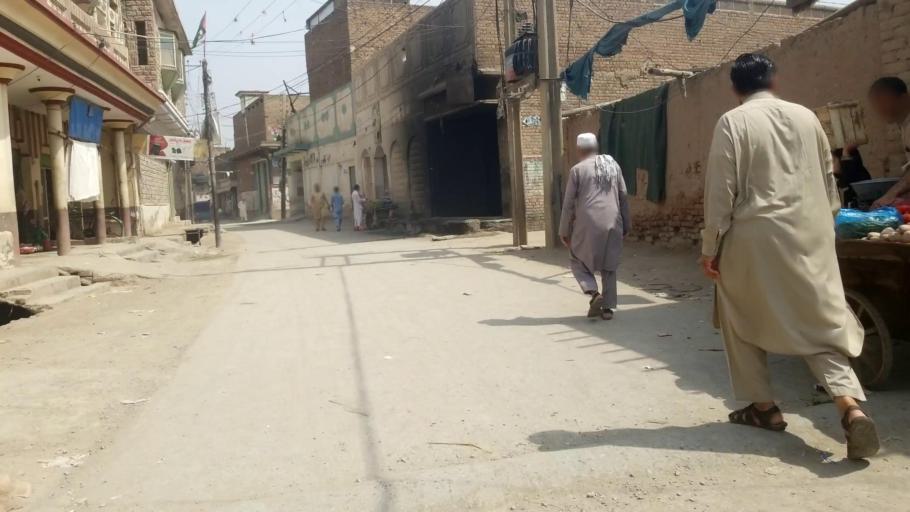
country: PK
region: Khyber Pakhtunkhwa
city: Peshawar
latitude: 33.9886
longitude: 71.5420
